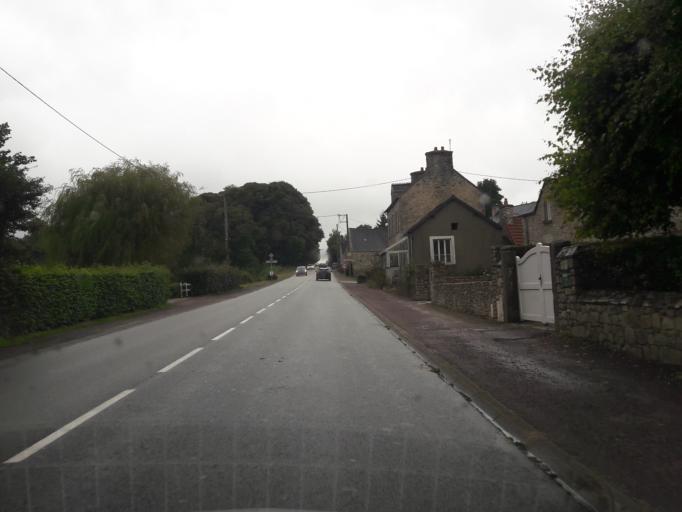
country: FR
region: Lower Normandy
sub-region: Departement de la Manche
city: Martinvast
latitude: 49.5684
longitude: -1.7273
